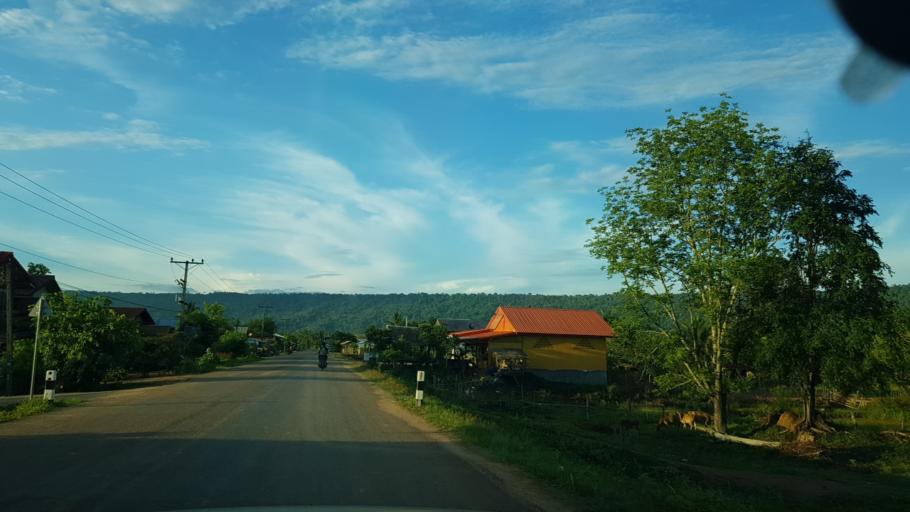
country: TH
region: Nong Khai
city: Sangkhom
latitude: 18.0942
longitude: 102.2867
